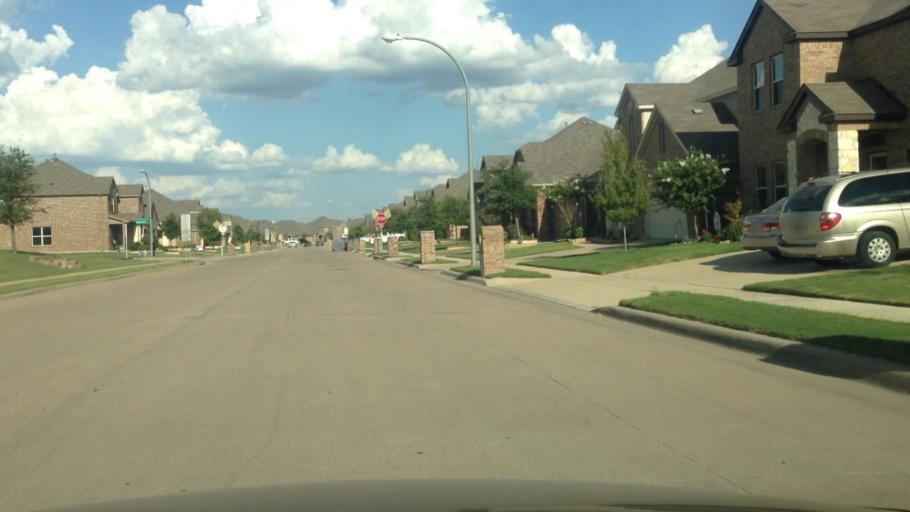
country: US
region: Texas
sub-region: Tarrant County
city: Haslet
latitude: 32.9374
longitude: -97.3866
